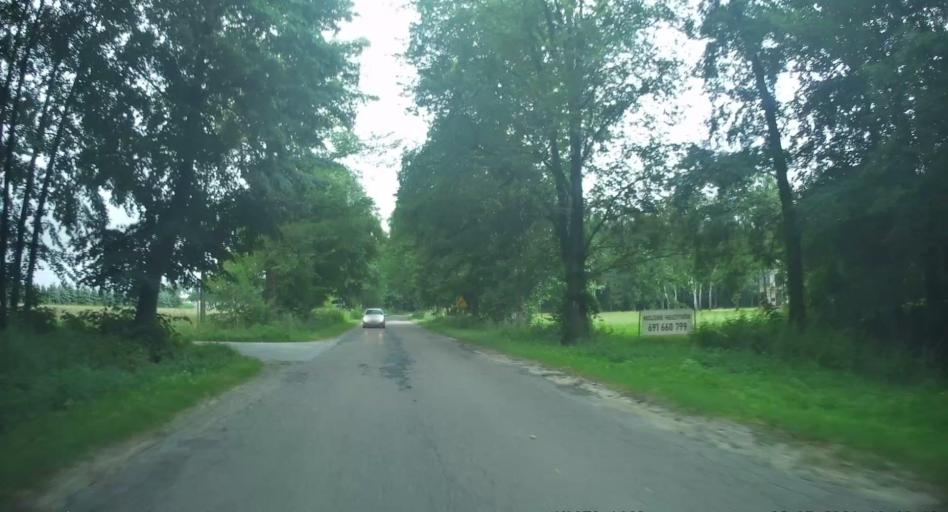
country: PL
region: Lodz Voivodeship
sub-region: Powiat rawski
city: Rawa Mazowiecka
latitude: 51.7462
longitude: 20.1859
